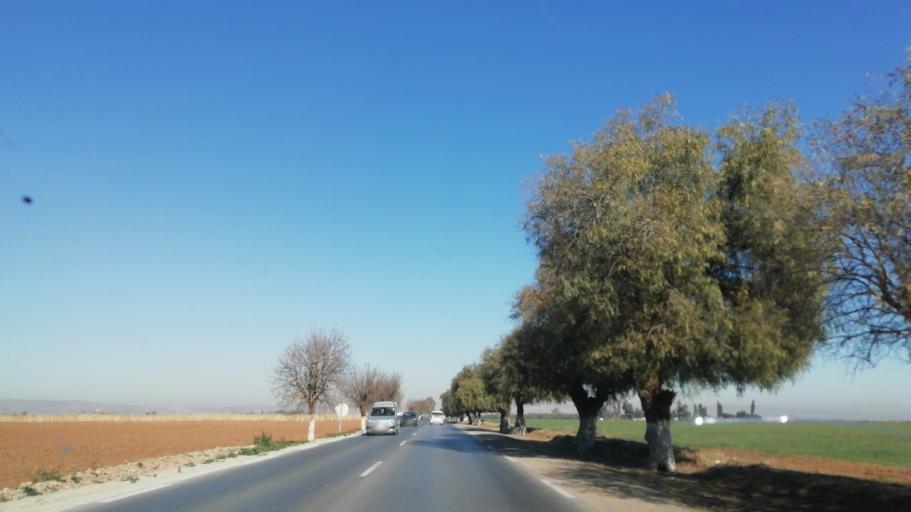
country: DZ
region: Mascara
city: Mascara
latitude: 35.2795
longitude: 0.1282
